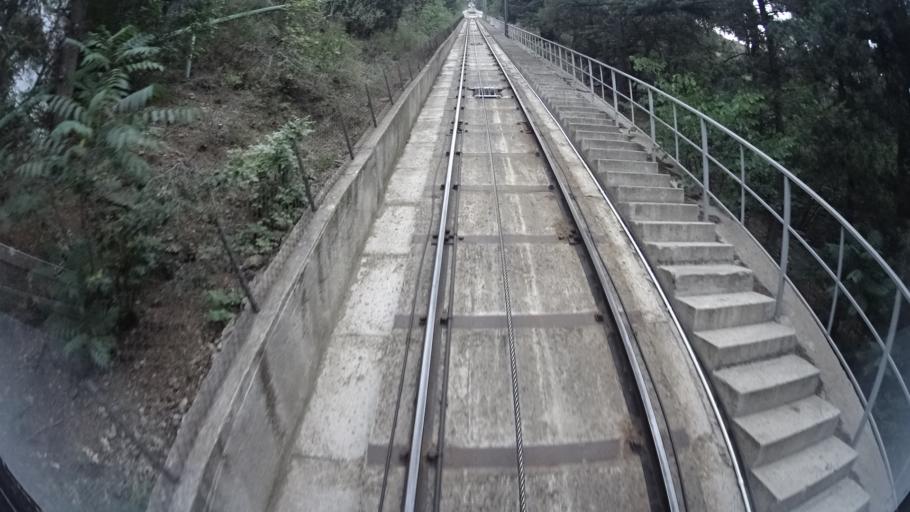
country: GE
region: T'bilisi
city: Tbilisi
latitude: 41.6951
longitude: 44.7906
